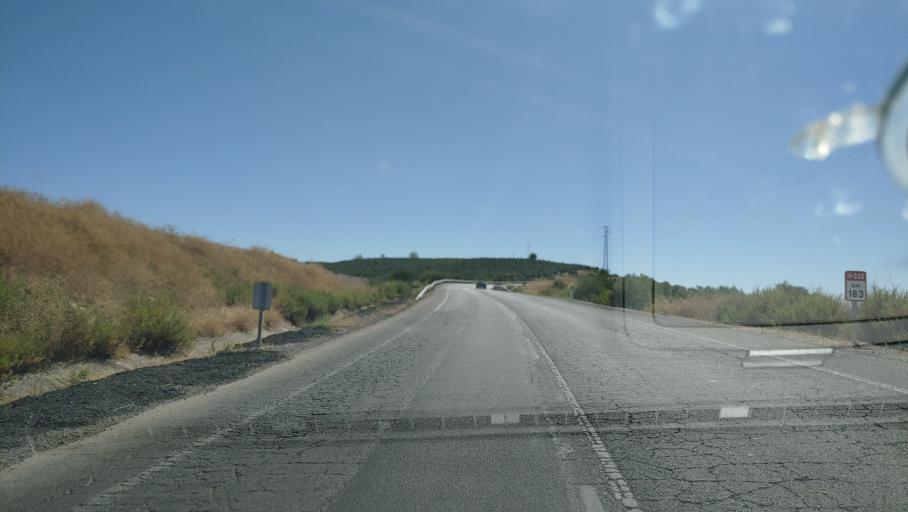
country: ES
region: Andalusia
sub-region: Provincia de Jaen
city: Iznatoraf
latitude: 38.1368
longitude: -3.0499
